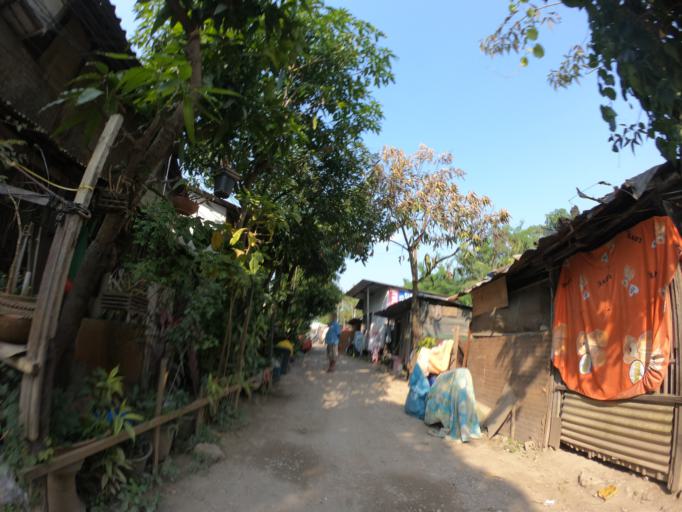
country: TH
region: Chiang Mai
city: Chiang Mai
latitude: 18.7686
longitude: 98.9903
